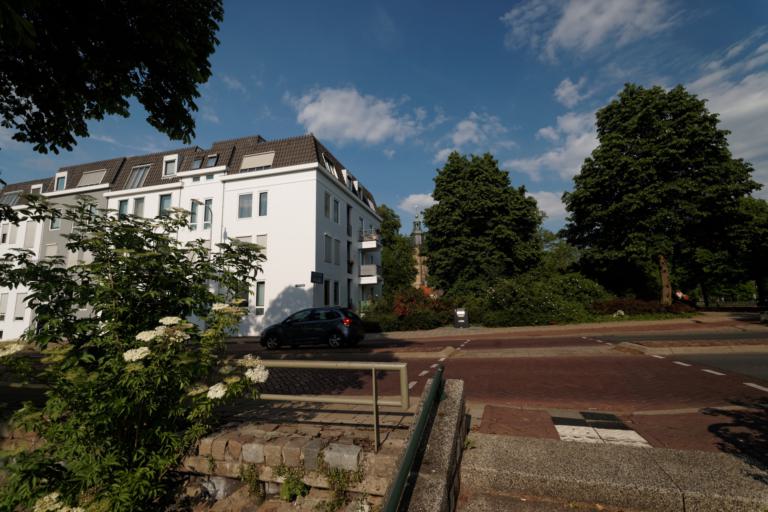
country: NL
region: Gelderland
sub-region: Gemeente Zutphen
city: Zutphen
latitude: 52.1388
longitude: 6.1918
